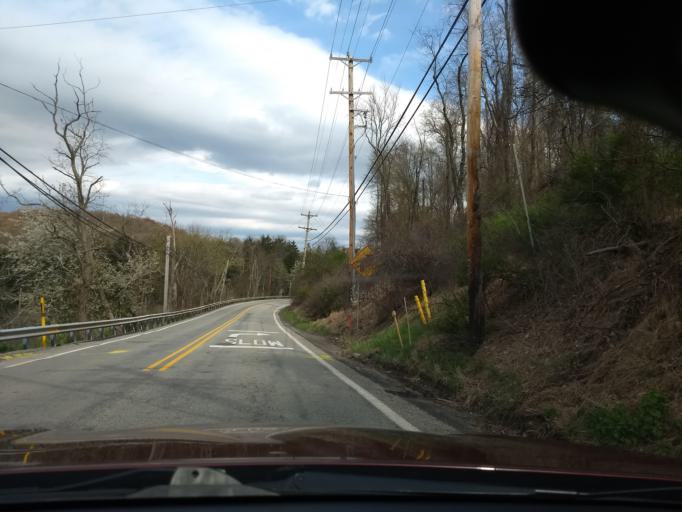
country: US
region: Pennsylvania
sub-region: Allegheny County
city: Allison Park
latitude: 40.5596
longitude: -79.9234
